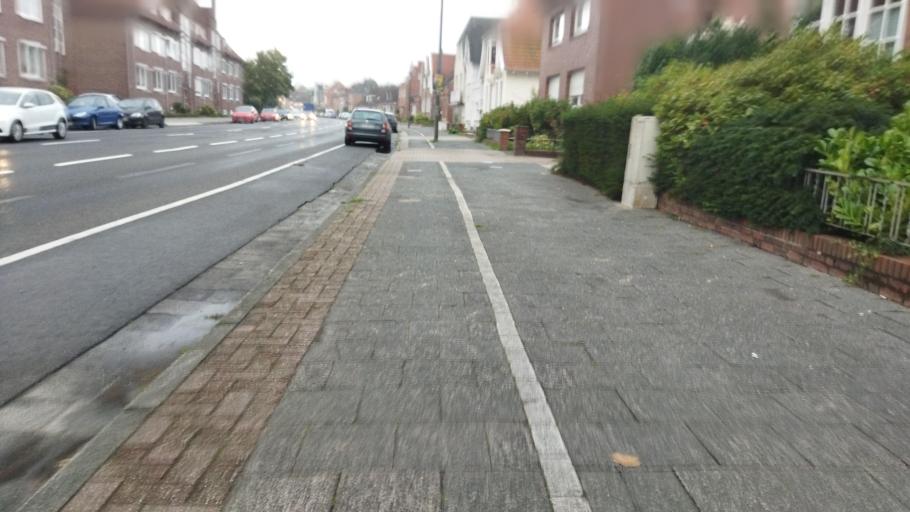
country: DE
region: Lower Saxony
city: Emden
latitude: 53.3791
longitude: 7.2063
